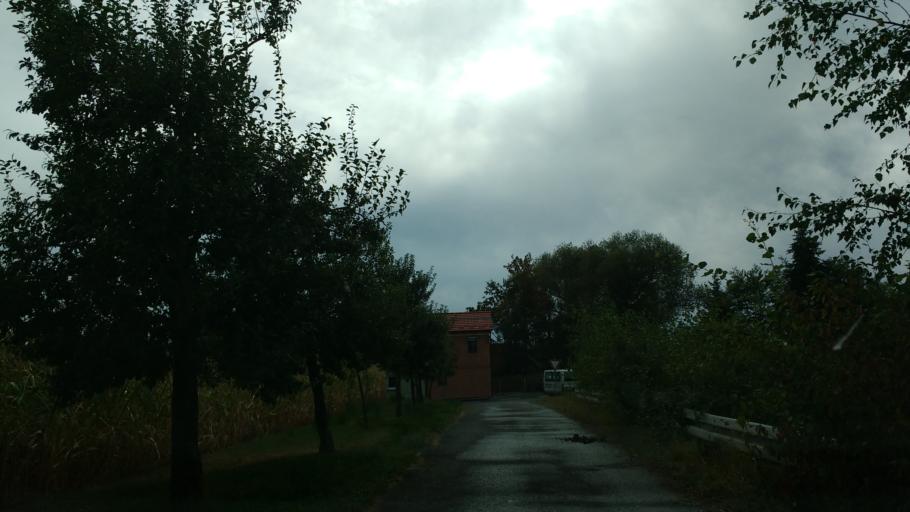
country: DE
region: Bavaria
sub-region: Regierungsbezirk Unterfranken
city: Geiselwind
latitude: 49.7967
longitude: 10.5100
